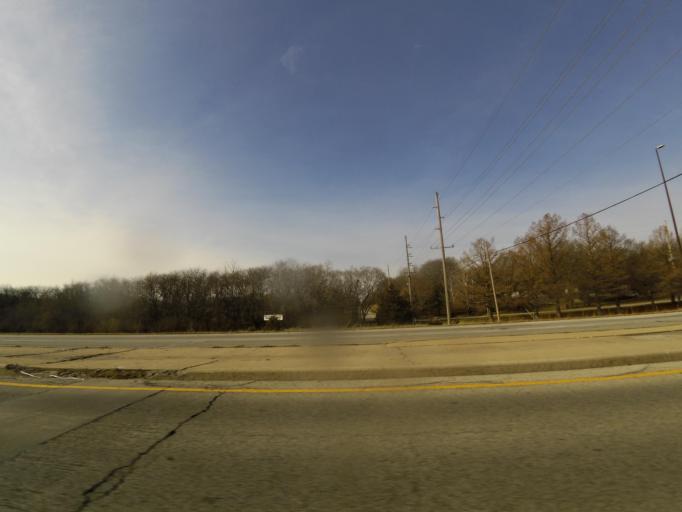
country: US
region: Illinois
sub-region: Macon County
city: Forsyth
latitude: 39.9130
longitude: -88.9553
